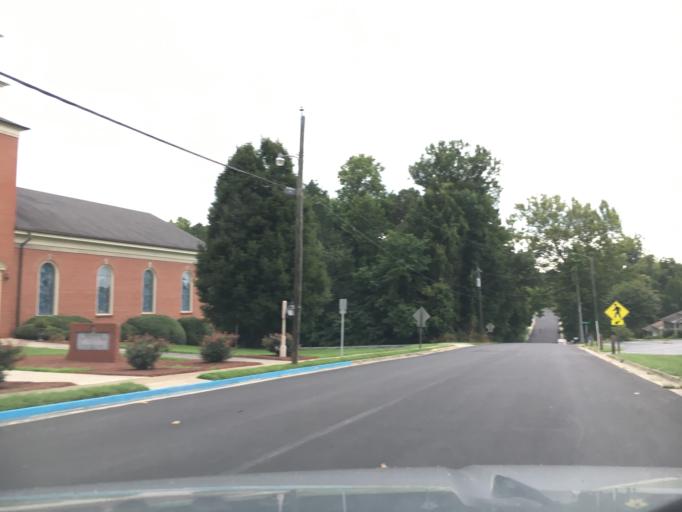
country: US
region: Virginia
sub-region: Halifax County
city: South Boston
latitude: 36.7003
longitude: -78.8868
